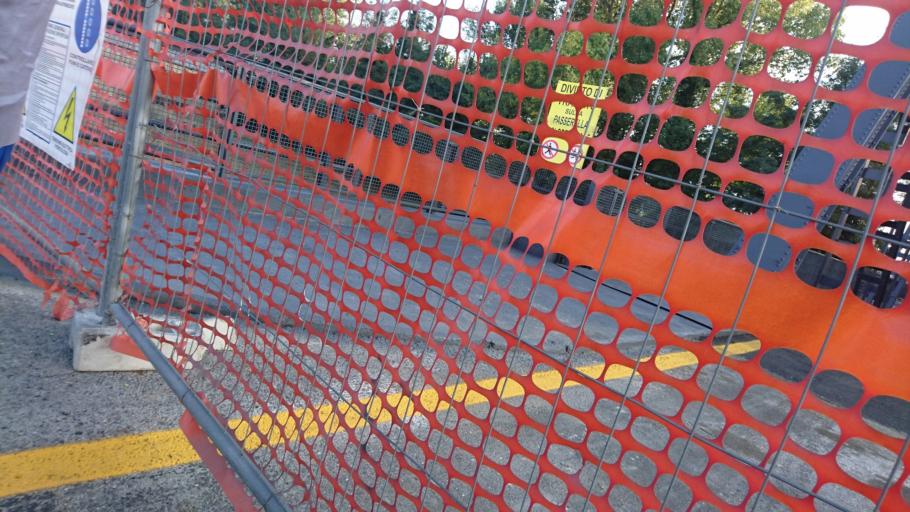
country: IT
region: Veneto
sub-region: Provincia di Rovigo
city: Santa Maria Maddalena
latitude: 44.8903
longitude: 11.6086
